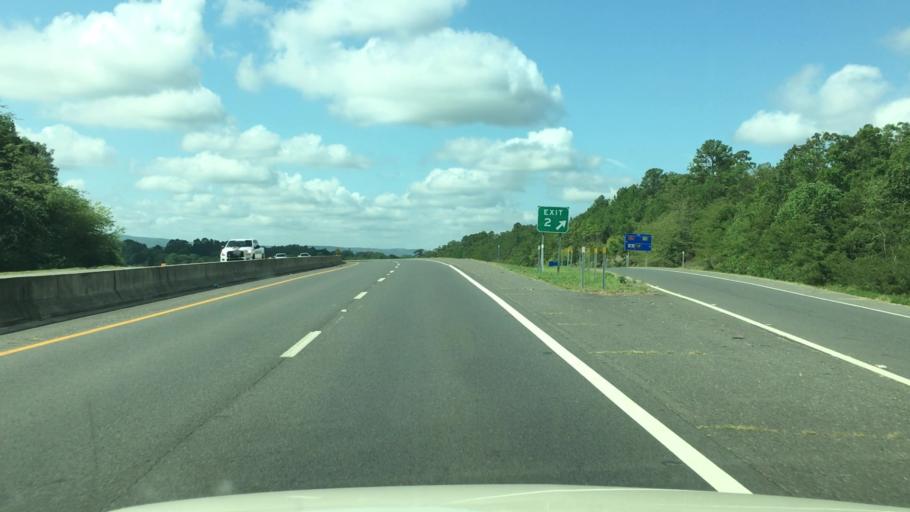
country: US
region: Arkansas
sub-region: Garland County
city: Piney
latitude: 34.4816
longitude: -93.1142
